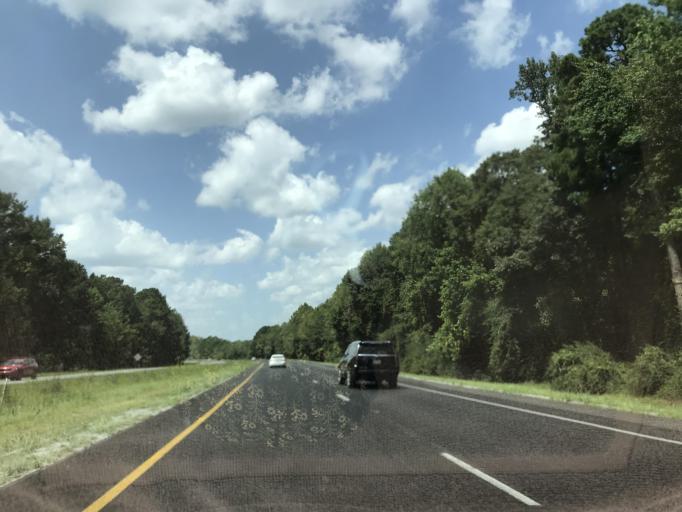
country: US
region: North Carolina
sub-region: Duplin County
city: Warsaw
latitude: 34.9420
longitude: -78.0597
